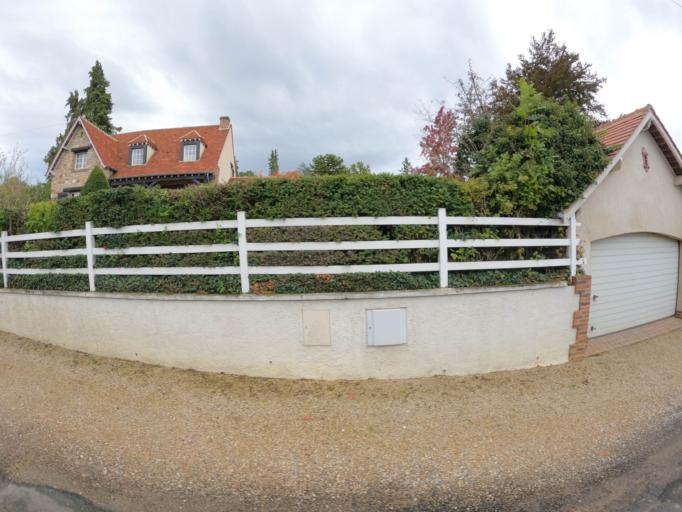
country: FR
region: Ile-de-France
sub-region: Departement de Seine-et-Marne
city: Saint-Germain-sur-Morin
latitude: 48.8729
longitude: 2.8447
